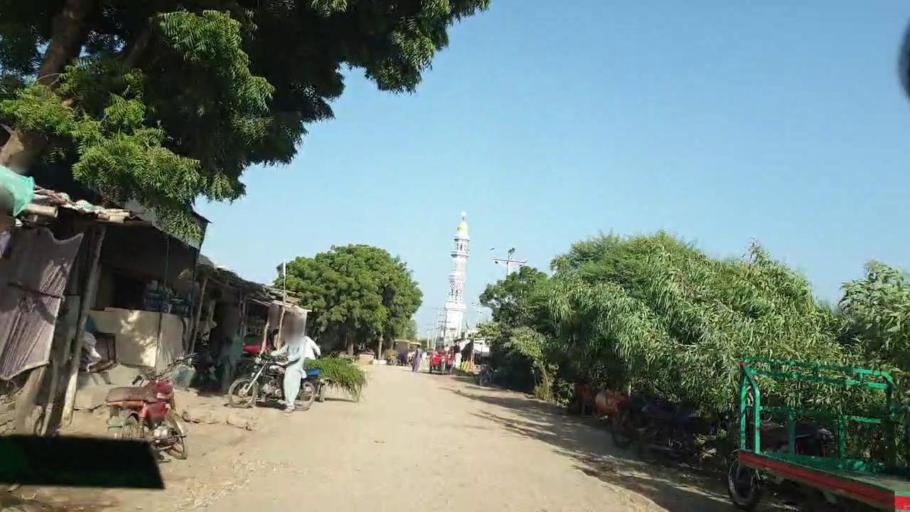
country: PK
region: Sindh
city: Naukot
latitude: 24.7408
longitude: 69.2253
